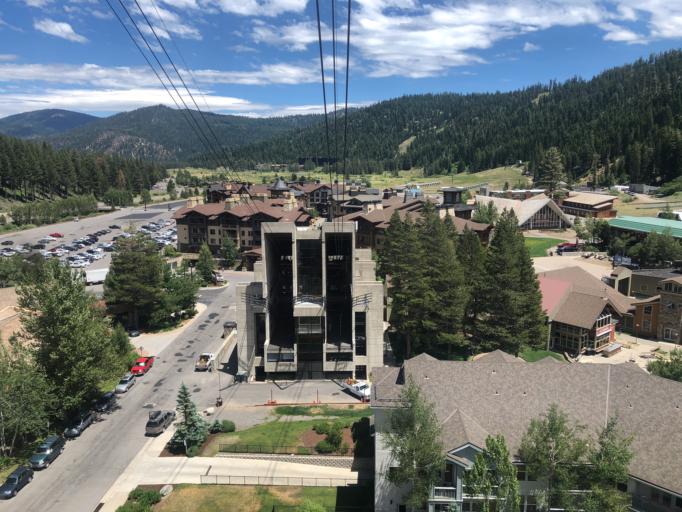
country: US
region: California
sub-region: Placer County
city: Sunnyside-Tahoe City
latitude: 39.1967
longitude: -120.2372
